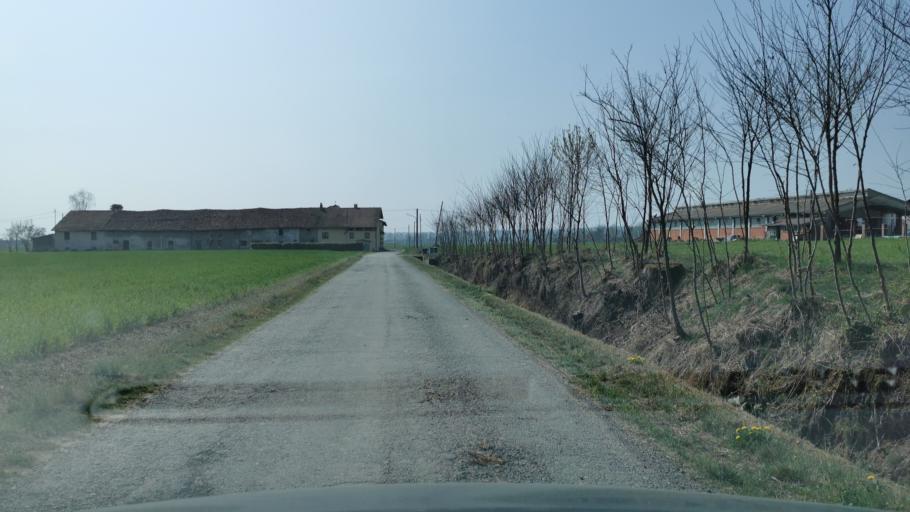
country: IT
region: Piedmont
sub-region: Provincia di Torino
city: Favria
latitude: 45.3033
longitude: 7.6943
